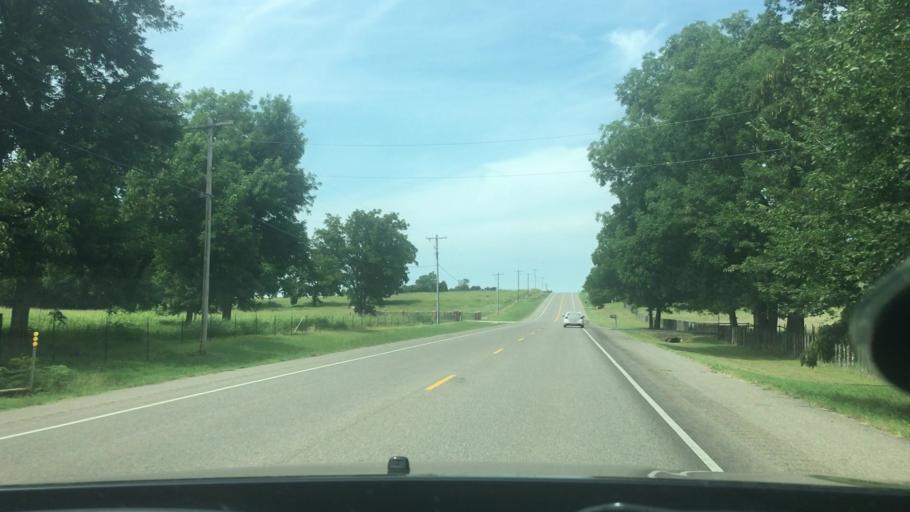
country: US
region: Oklahoma
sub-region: Pottawatomie County
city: Shawnee
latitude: 35.3331
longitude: -96.8157
